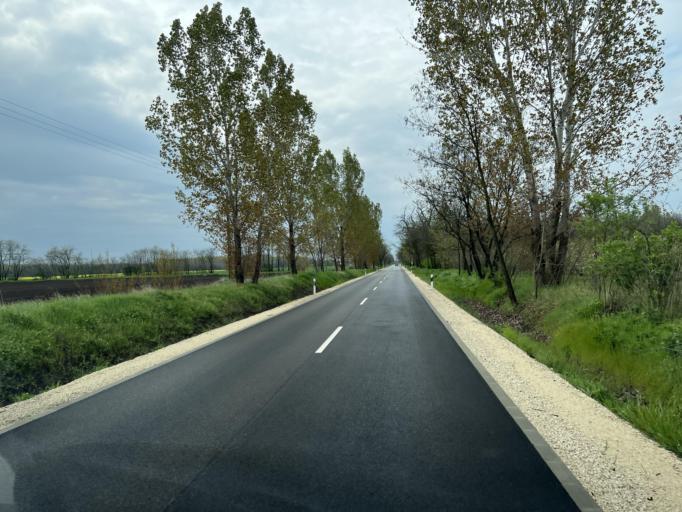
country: HU
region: Pest
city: Nyaregyhaza
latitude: 47.2364
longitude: 19.5196
